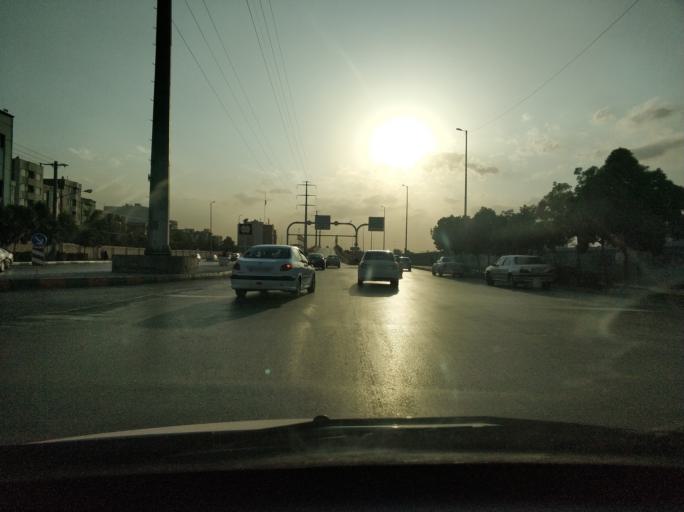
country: IR
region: Razavi Khorasan
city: Mashhad
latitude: 36.3394
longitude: 59.5515
